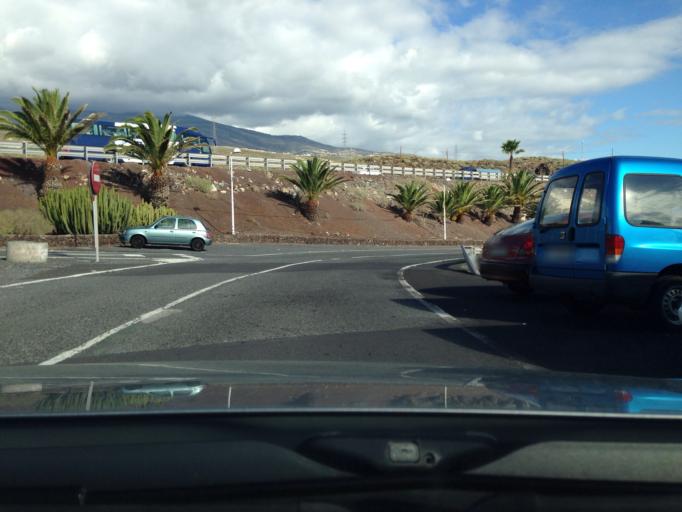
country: ES
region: Canary Islands
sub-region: Provincia de Santa Cruz de Tenerife
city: Fasnia
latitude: 28.2230
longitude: -16.4139
